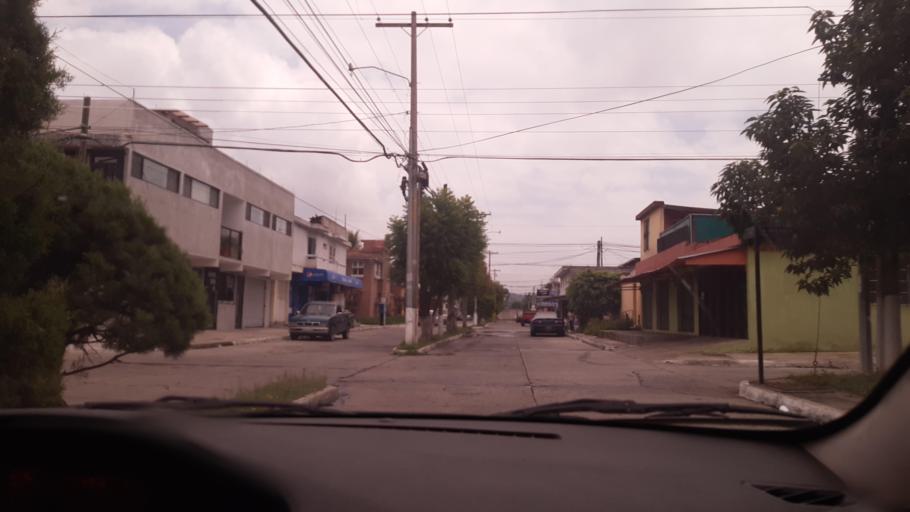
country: GT
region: Guatemala
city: Petapa
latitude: 14.5069
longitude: -90.5459
